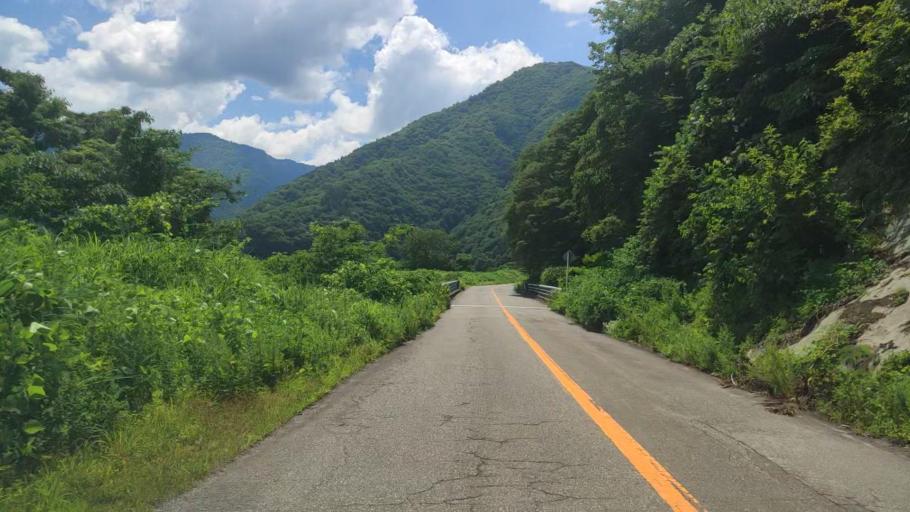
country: JP
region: Fukui
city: Ono
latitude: 35.9070
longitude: 136.5316
